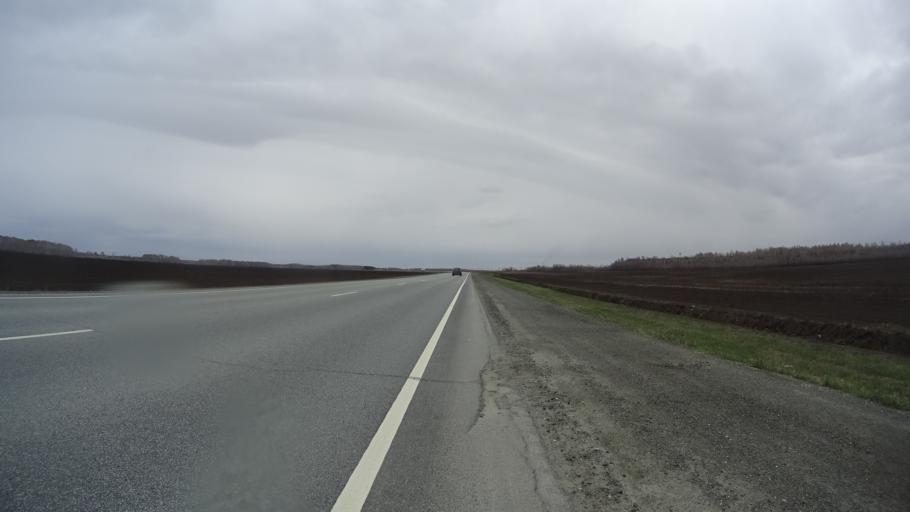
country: RU
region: Chelyabinsk
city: Krasnogorskiy
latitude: 54.5717
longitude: 61.2906
